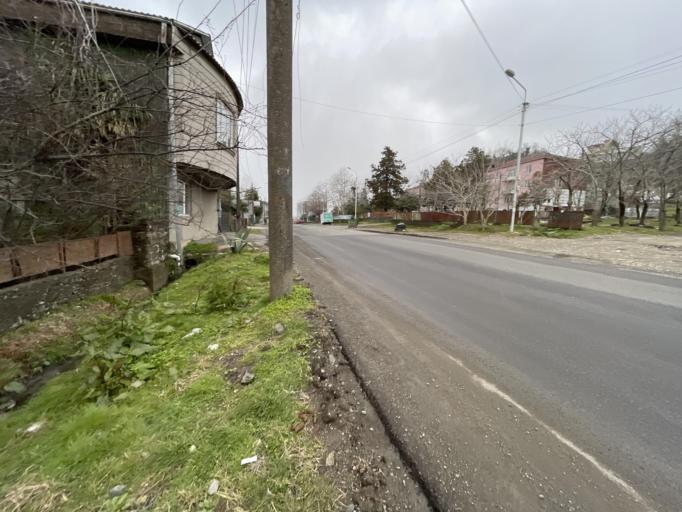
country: GE
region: Ajaria
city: Batumi
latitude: 41.6347
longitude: 41.6450
